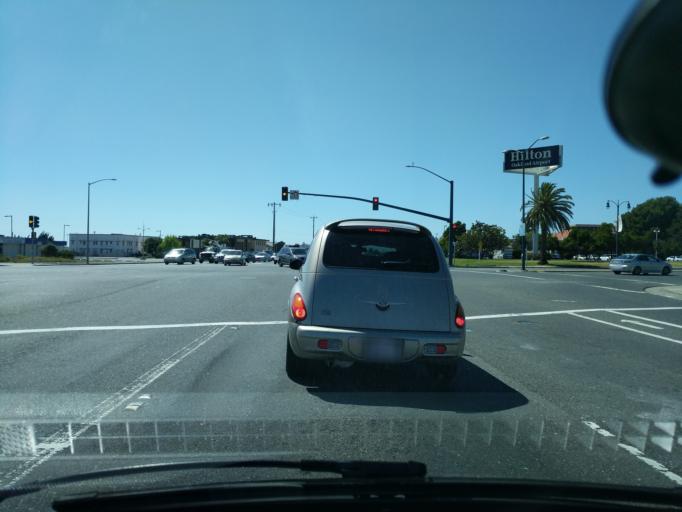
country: US
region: California
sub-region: Alameda County
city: San Leandro
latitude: 37.7265
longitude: -122.2012
